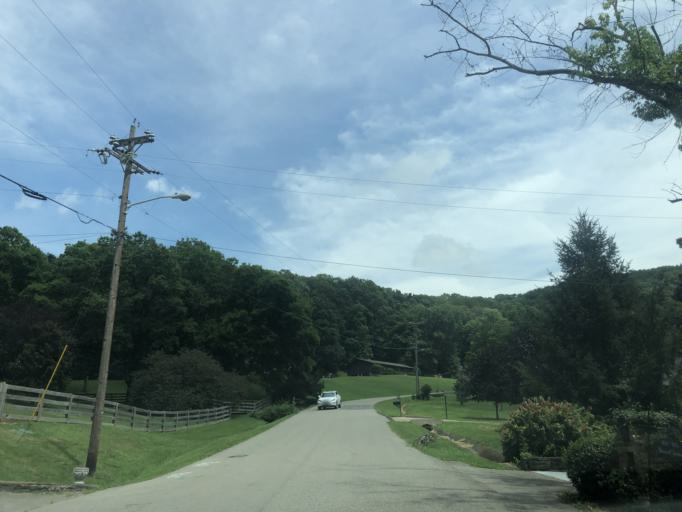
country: US
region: Tennessee
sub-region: Davidson County
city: Oak Hill
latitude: 36.0693
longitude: -86.8093
